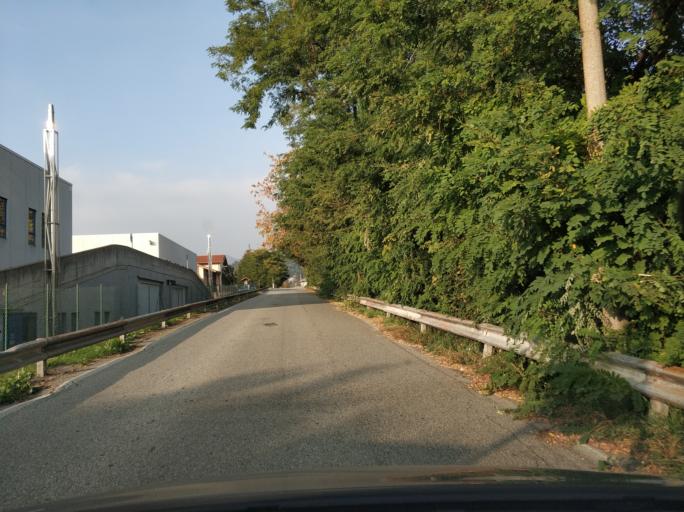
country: IT
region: Piedmont
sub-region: Provincia di Biella
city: Biella
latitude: 45.5664
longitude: 8.0726
